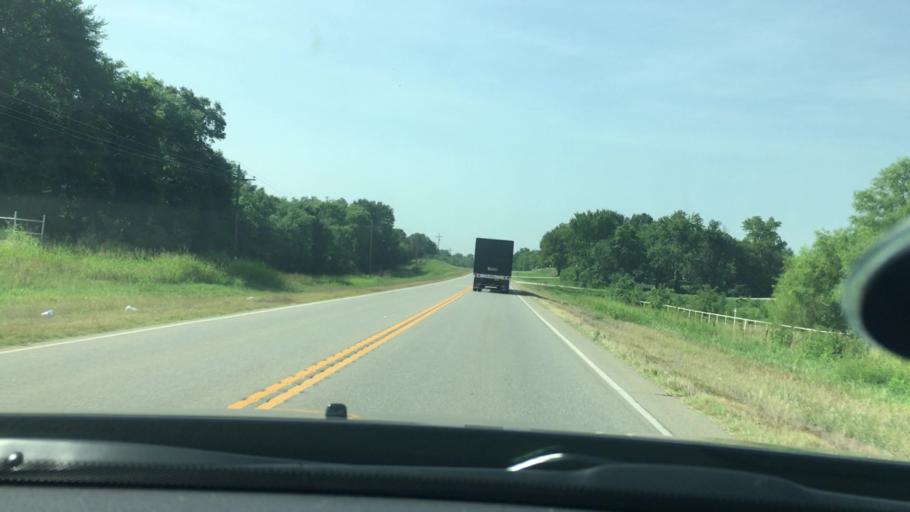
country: US
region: Oklahoma
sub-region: Coal County
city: Coalgate
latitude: 34.5025
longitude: -96.2197
